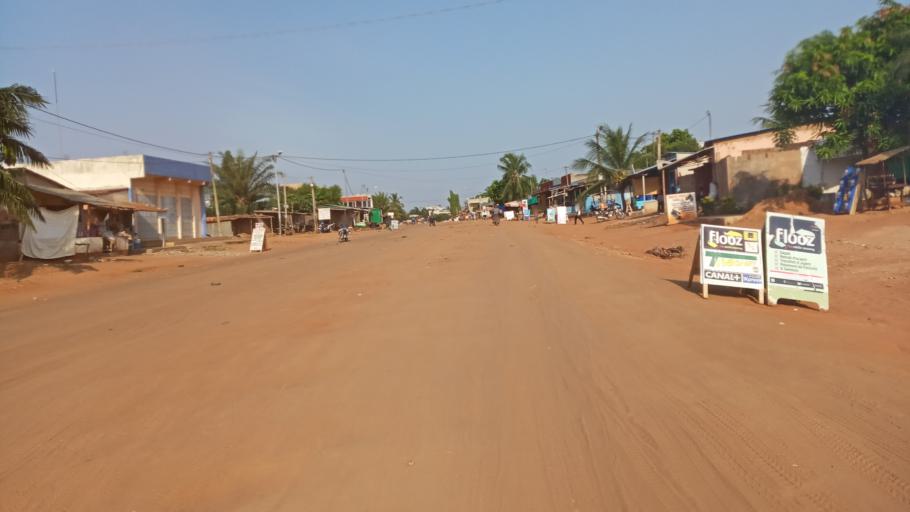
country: TG
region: Maritime
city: Lome
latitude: 6.1802
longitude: 1.1530
